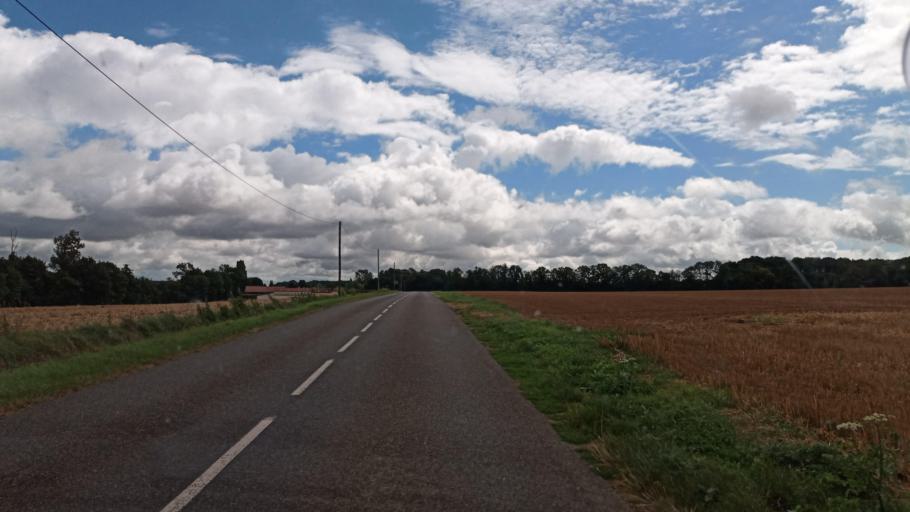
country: FR
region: Bourgogne
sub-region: Departement de l'Yonne
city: Cheroy
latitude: 48.2452
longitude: 3.0365
